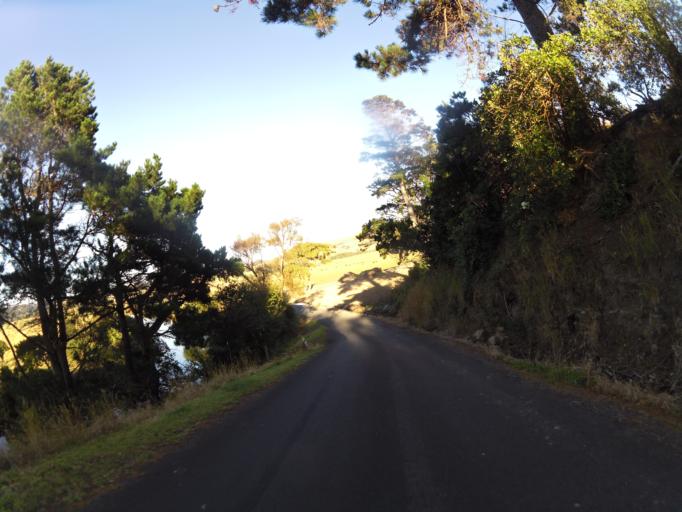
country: AU
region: Victoria
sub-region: Colac-Otway
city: Apollo Bay
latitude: -38.7609
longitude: 143.6646
